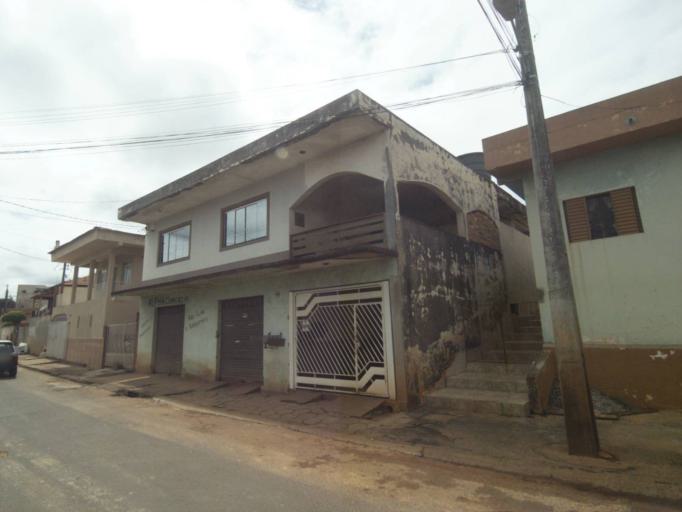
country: BR
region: Parana
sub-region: Telemaco Borba
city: Telemaco Borba
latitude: -24.3273
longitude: -50.6312
